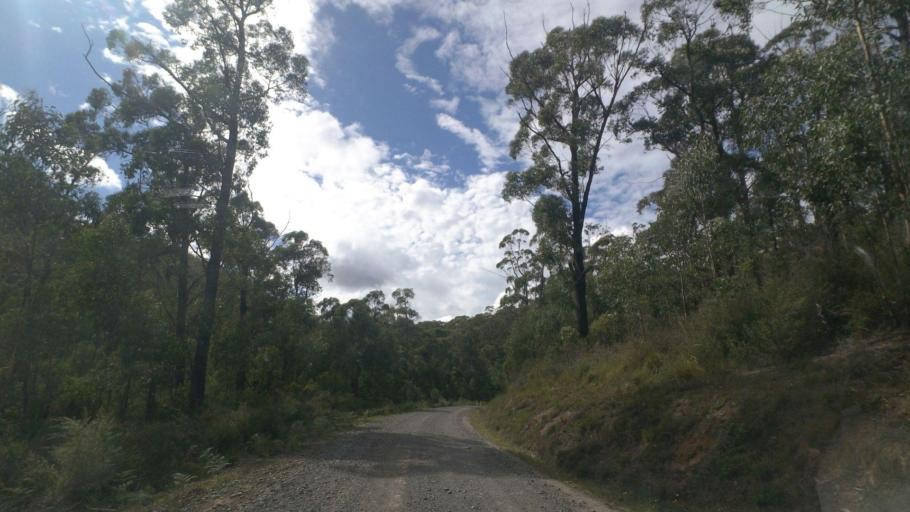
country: AU
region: Victoria
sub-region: Cardinia
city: Bunyip
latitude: -37.9829
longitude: 145.8160
